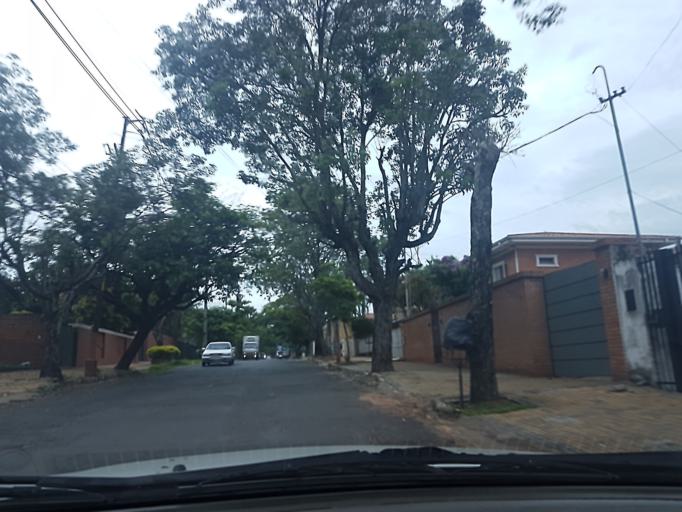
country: PY
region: Asuncion
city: Asuncion
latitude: -25.2999
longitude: -57.5962
